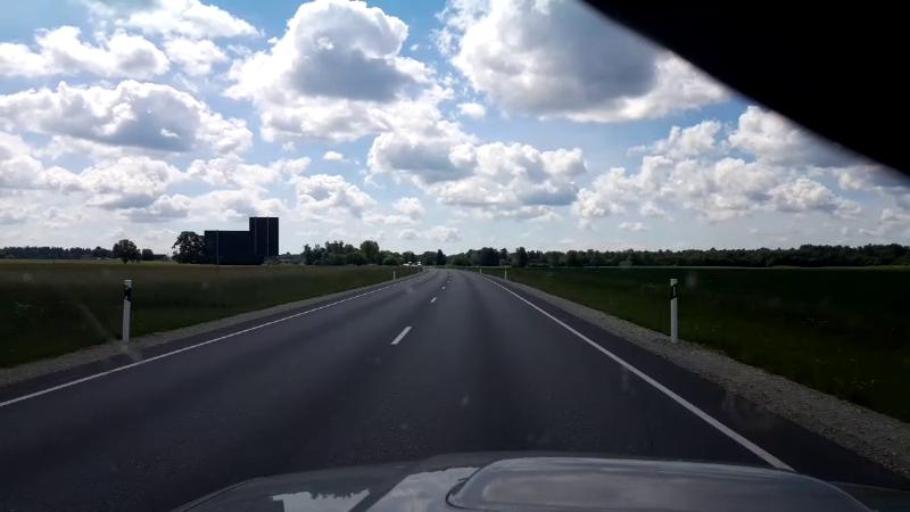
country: EE
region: Jaervamaa
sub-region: Jaerva-Jaani vald
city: Jarva-Jaani
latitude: 59.0804
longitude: 25.6836
